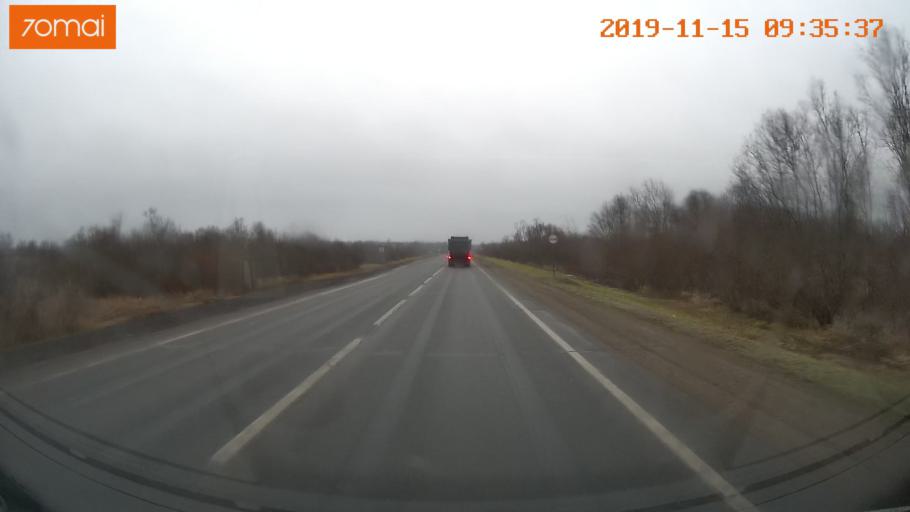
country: RU
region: Vologda
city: Sheksna
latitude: 59.2532
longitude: 38.4032
